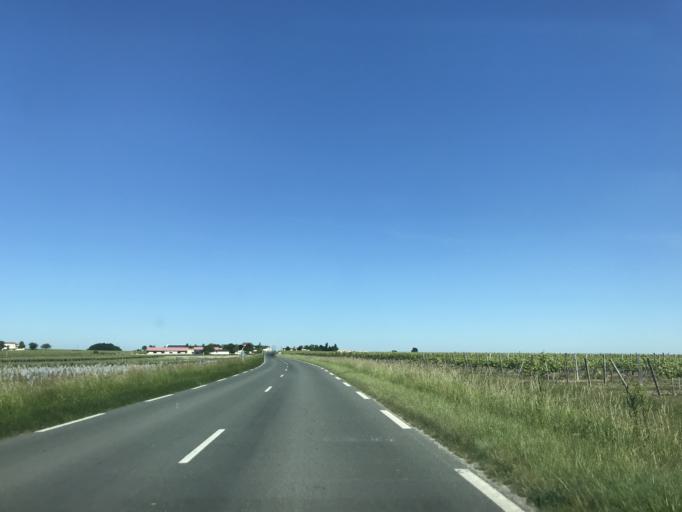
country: FR
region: Poitou-Charentes
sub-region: Departement de la Charente-Maritime
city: Perignac
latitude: 45.5545
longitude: -0.3731
